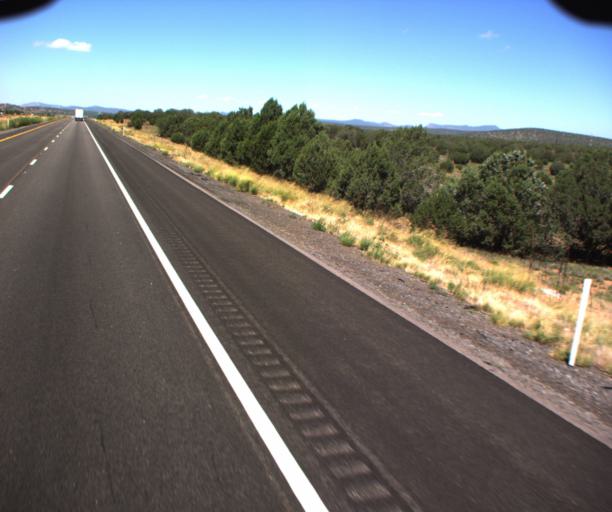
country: US
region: Arizona
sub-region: Mohave County
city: Peach Springs
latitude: 35.1912
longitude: -113.3440
